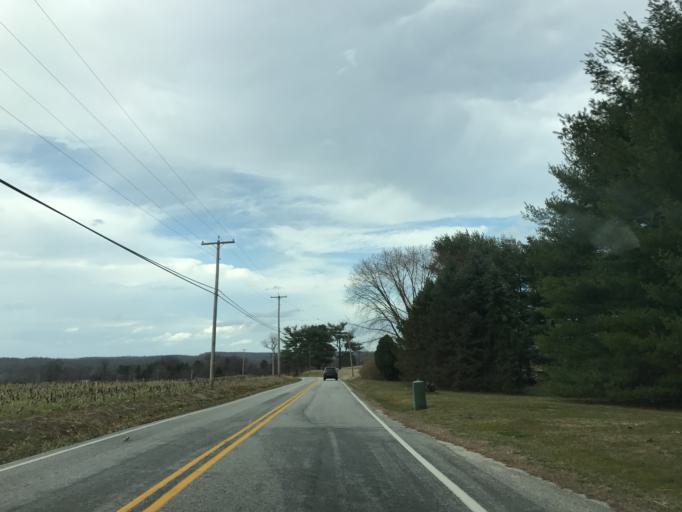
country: US
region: Maryland
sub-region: Harford County
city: South Bel Air
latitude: 39.5814
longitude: -76.2816
